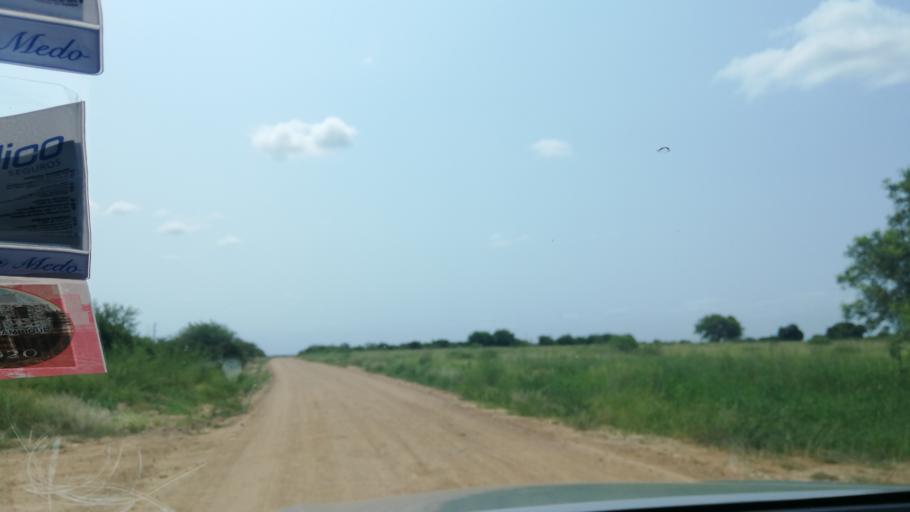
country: MZ
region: Maputo
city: Matola
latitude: -26.0858
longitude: 32.3915
